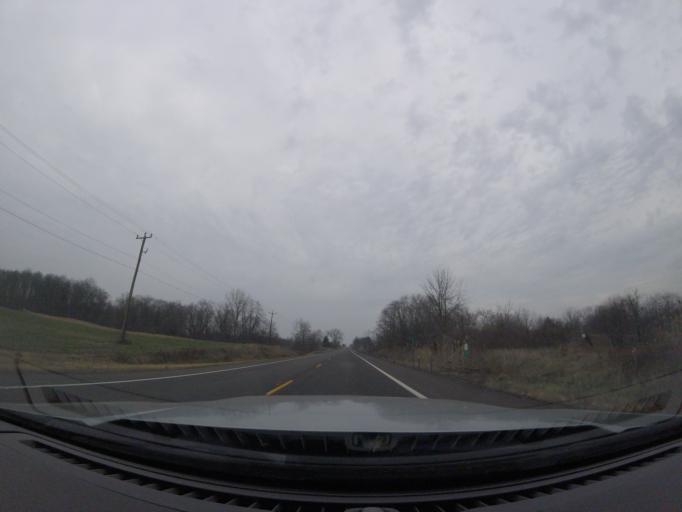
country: US
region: New York
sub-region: Yates County
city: Dundee
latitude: 42.6095
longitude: -76.9439
